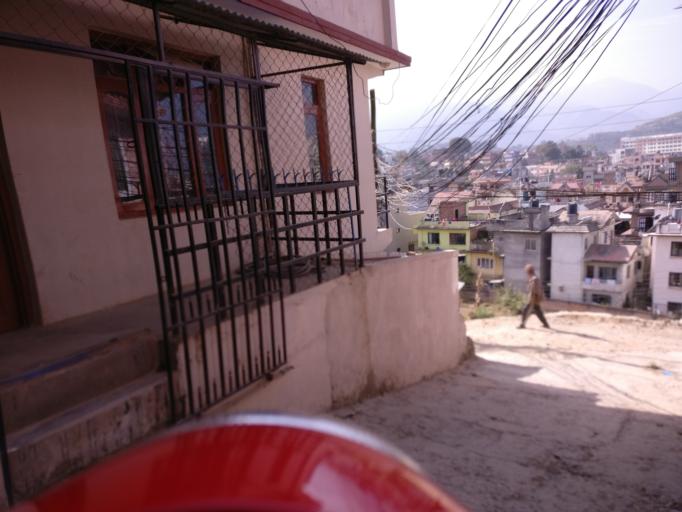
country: NP
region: Central Region
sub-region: Bagmati Zone
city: Patan
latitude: 27.6612
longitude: 85.3101
